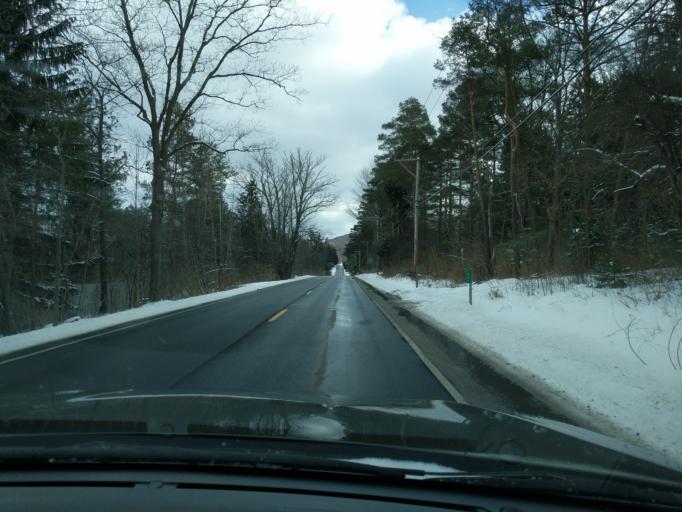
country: US
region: New York
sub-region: Tompkins County
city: Northeast Ithaca
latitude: 42.4290
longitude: -76.4195
